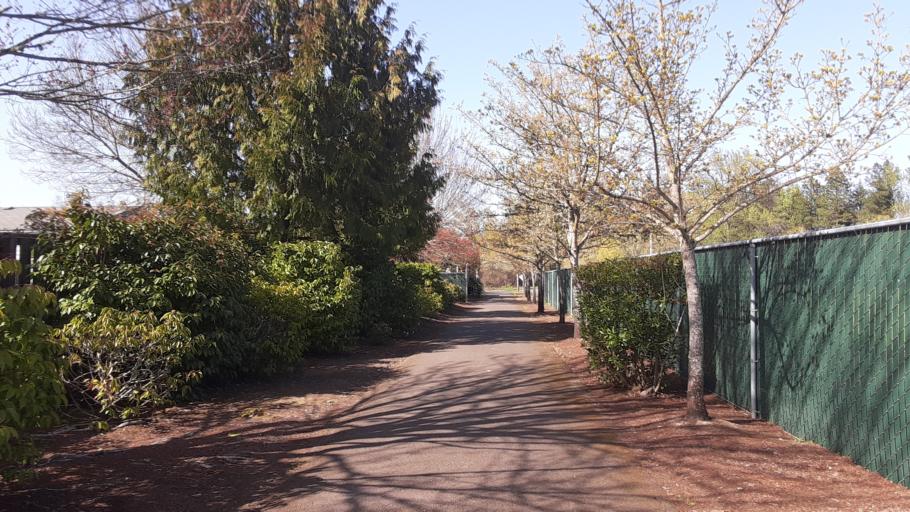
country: US
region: Oregon
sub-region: Benton County
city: Corvallis
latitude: 44.5360
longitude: -123.2539
